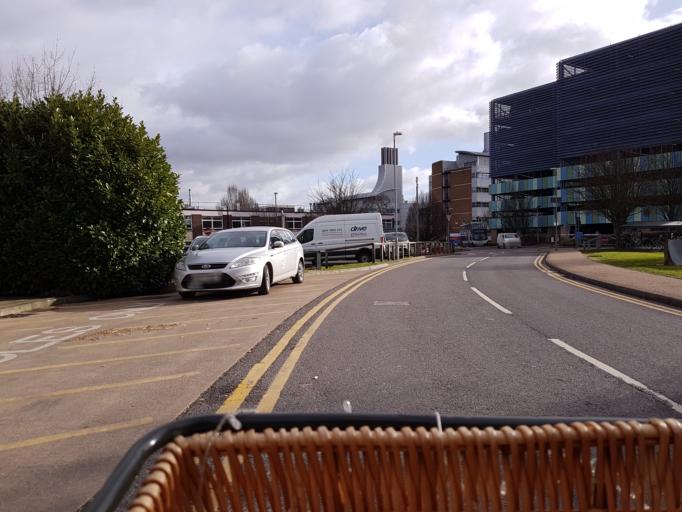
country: GB
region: England
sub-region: Cambridgeshire
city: Cambridge
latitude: 52.1774
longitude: 0.1394
